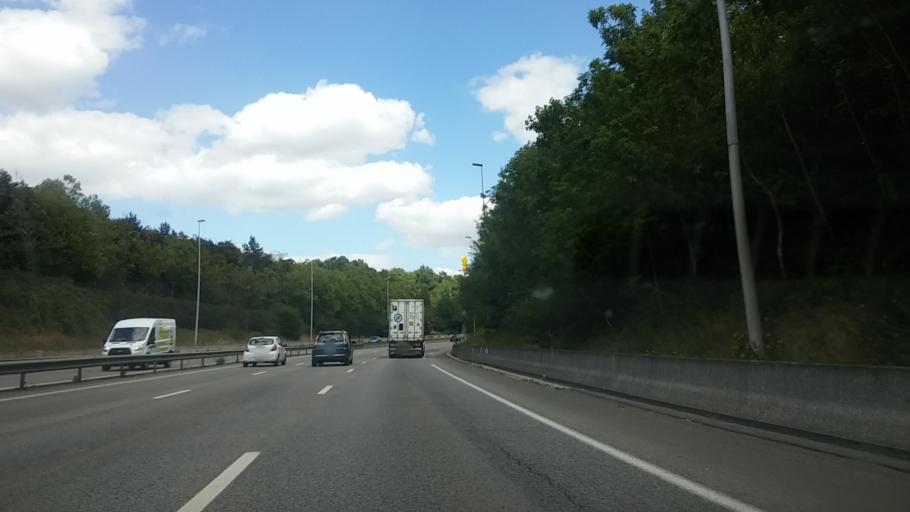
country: FR
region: Ile-de-France
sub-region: Departement des Yvelines
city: Saint-Cyr-l'Ecole
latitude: 48.7914
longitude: 2.0719
